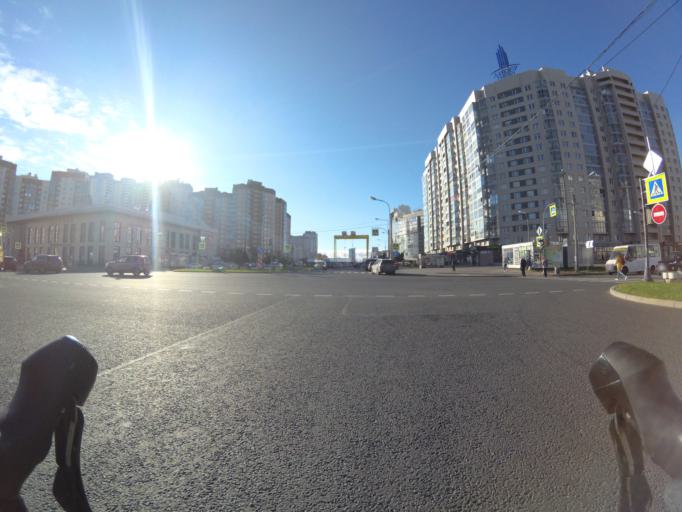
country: RU
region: Leningrad
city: Untolovo
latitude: 60.0016
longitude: 30.2093
